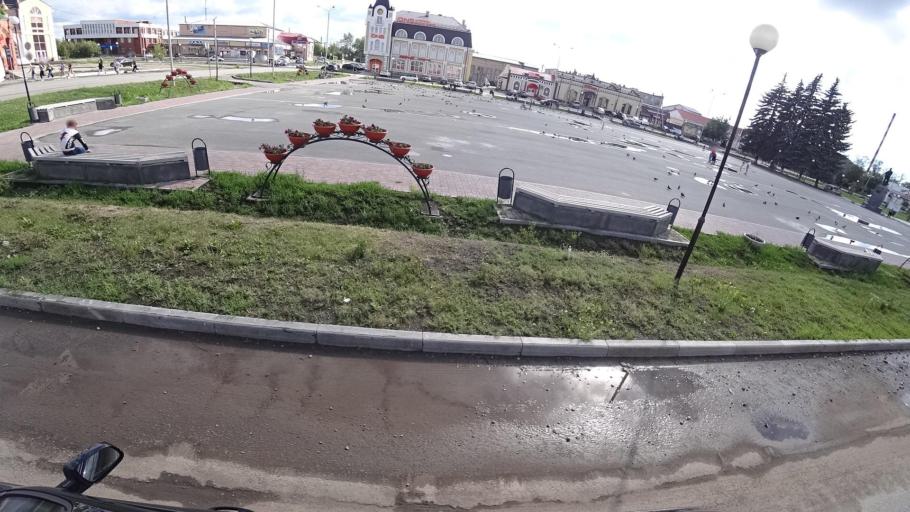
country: RU
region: Sverdlovsk
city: Kamyshlov
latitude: 56.8441
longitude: 62.7082
